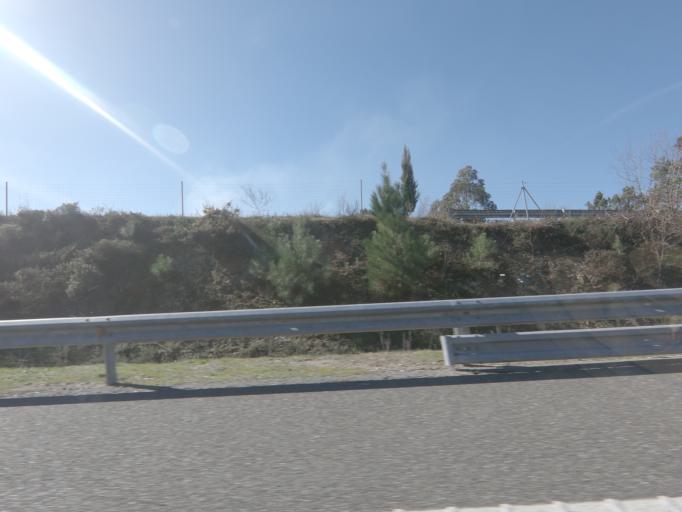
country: ES
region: Galicia
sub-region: Provincia de Ourense
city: Maside
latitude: 42.4324
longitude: -8.0160
